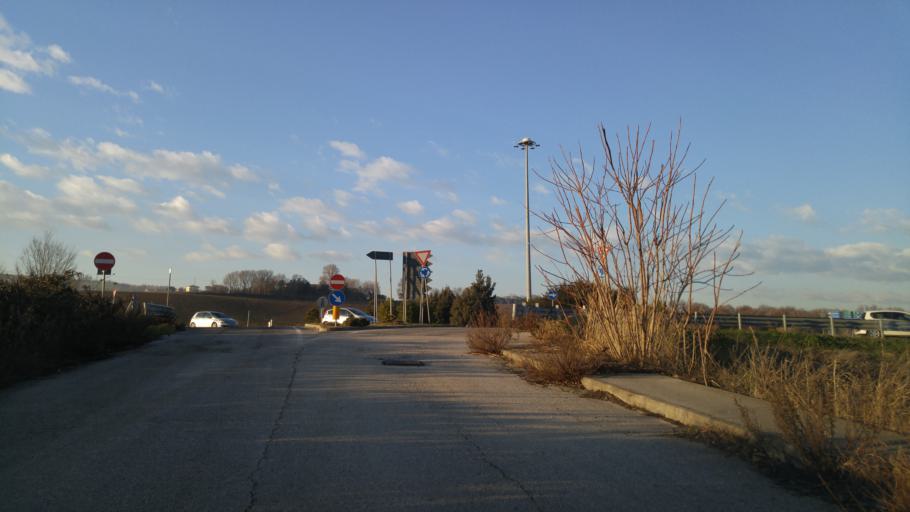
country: IT
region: The Marches
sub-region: Provincia di Ancona
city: Monterado
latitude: 43.7095
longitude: 13.0749
